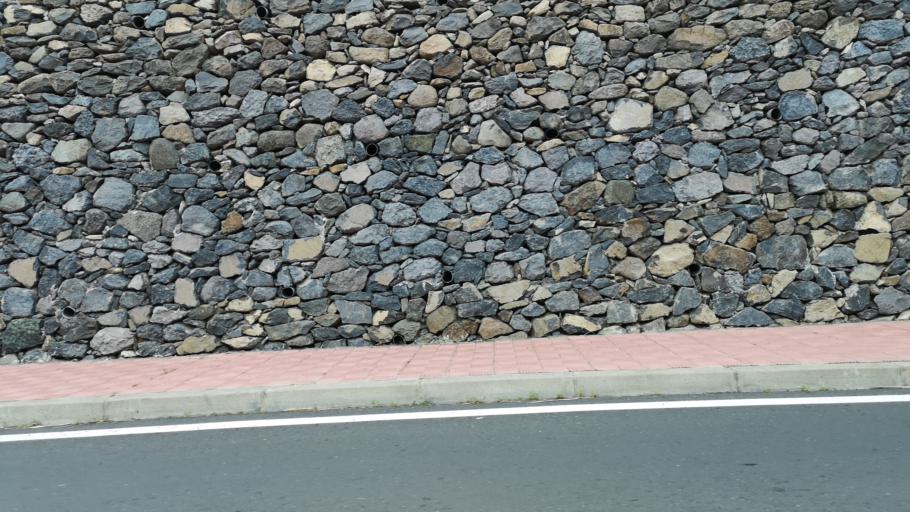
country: ES
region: Canary Islands
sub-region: Provincia de Santa Cruz de Tenerife
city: Hermigua
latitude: 28.1596
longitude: -17.1984
